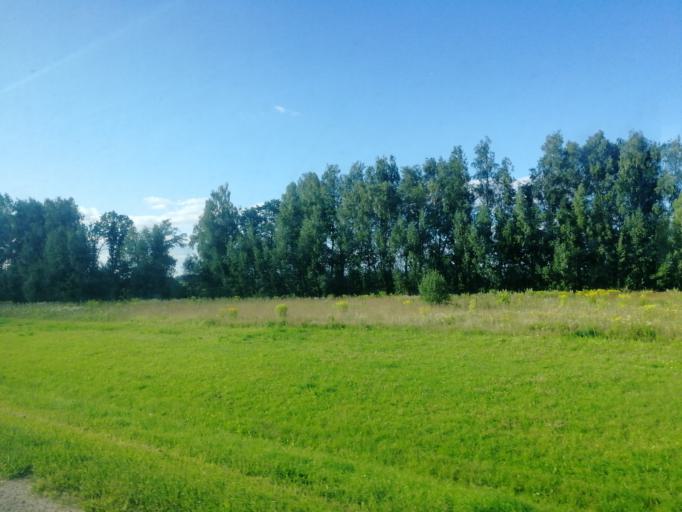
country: RU
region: Tula
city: Leninskiy
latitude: 54.2378
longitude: 37.3468
